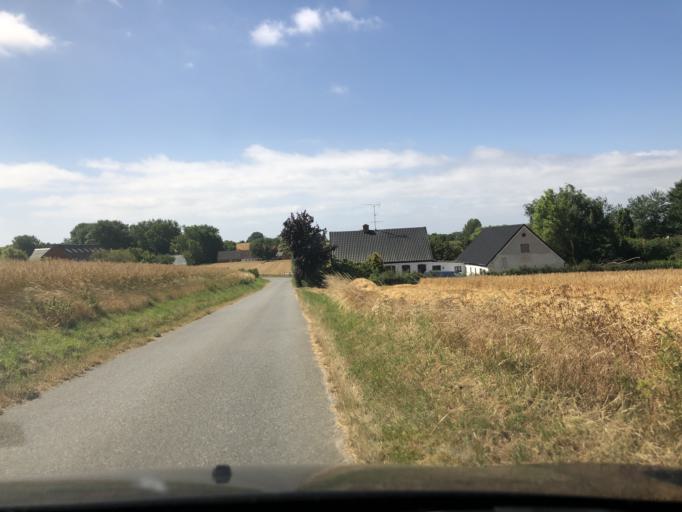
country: DK
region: South Denmark
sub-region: AEro Kommune
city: AEroskobing
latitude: 54.9186
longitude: 10.2960
